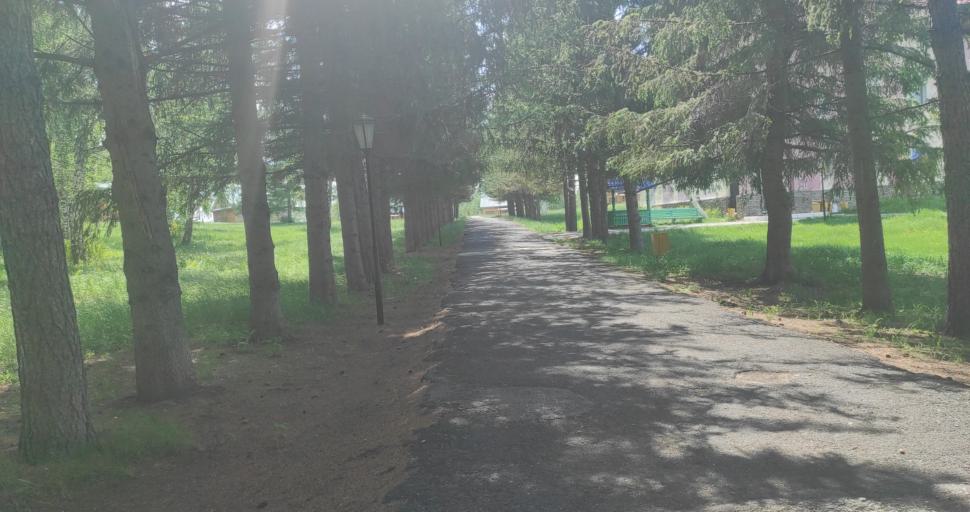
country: RU
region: Bashkortostan
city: Tubinskiy
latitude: 52.8127
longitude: 58.2525
